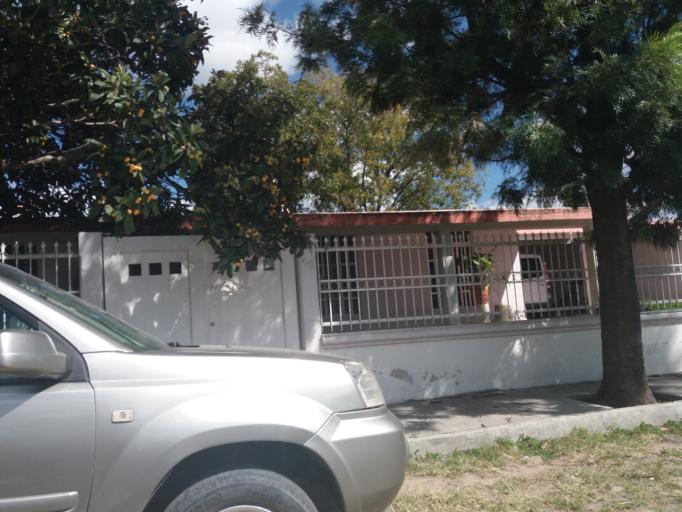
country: MX
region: Aguascalientes
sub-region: Aguascalientes
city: San Sebastian [Fraccionamiento]
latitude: 21.7914
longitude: -102.2783
